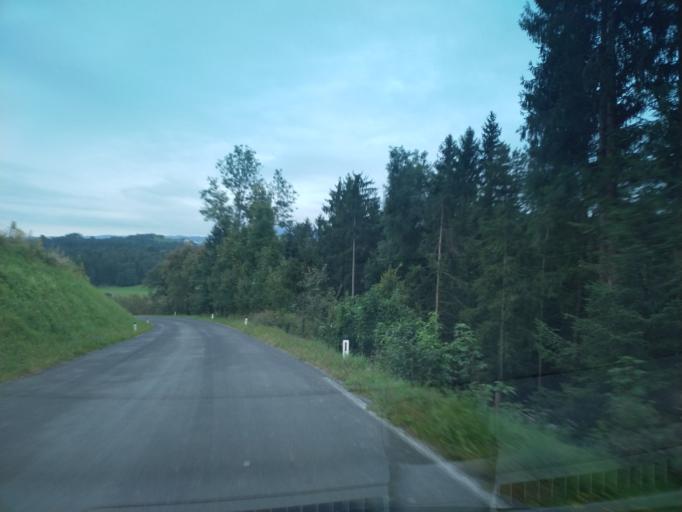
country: AT
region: Styria
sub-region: Politischer Bezirk Deutschlandsberg
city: Wernersdorf
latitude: 46.7168
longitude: 15.2015
